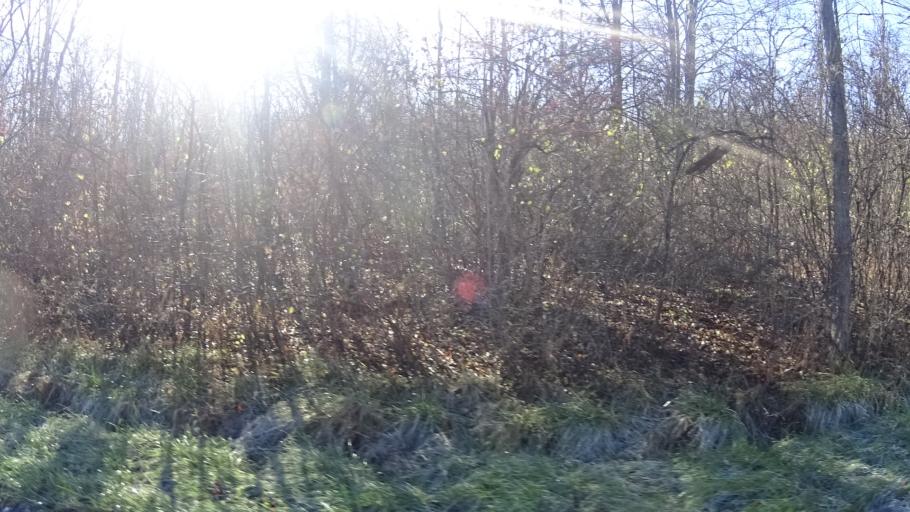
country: US
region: Ohio
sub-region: Lorain County
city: Sheffield Lake
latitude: 41.4600
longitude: -82.1143
